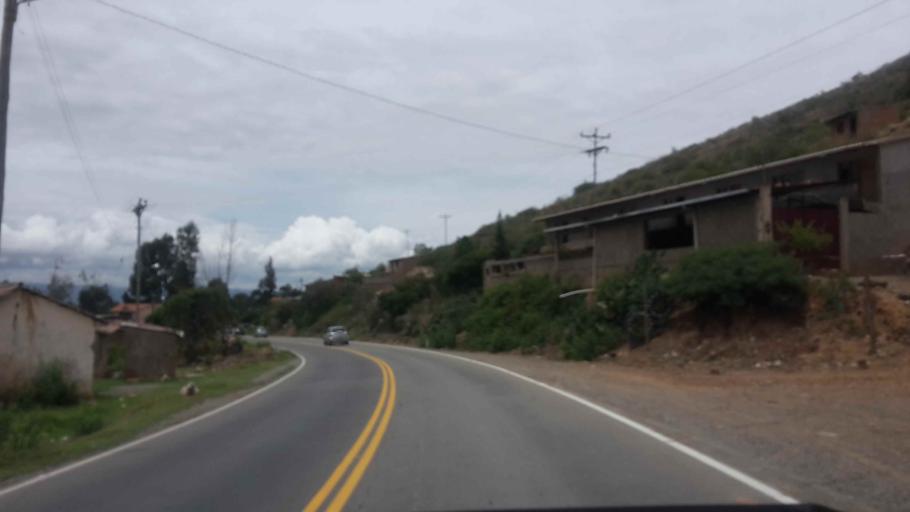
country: BO
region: Cochabamba
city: Punata
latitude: -17.5141
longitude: -65.8158
